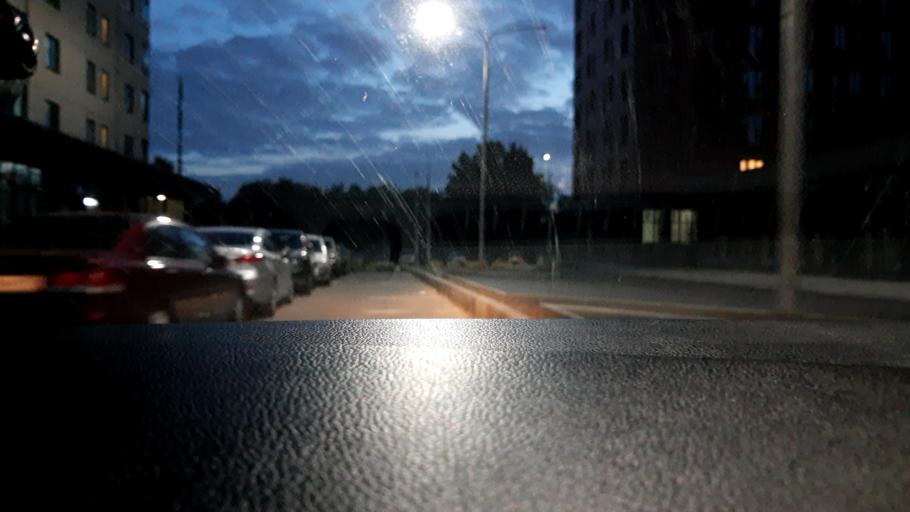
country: RU
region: Moscow
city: Ryazanskiy
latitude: 55.7253
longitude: 37.7453
